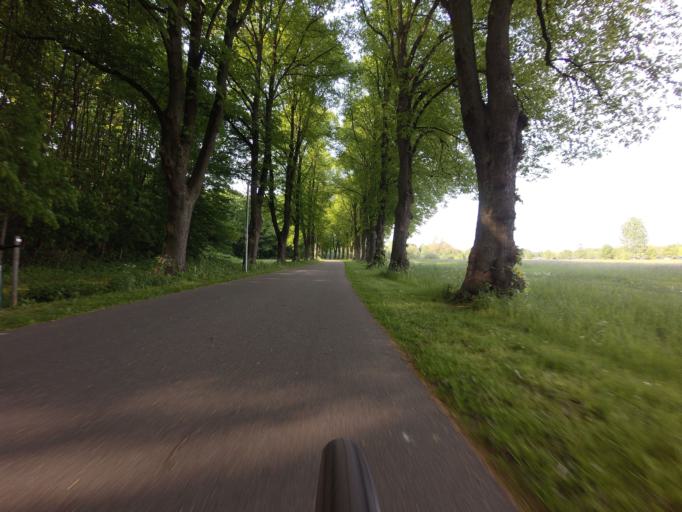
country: DK
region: Capital Region
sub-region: Glostrup Kommune
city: Glostrup
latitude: 55.6711
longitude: 12.4265
